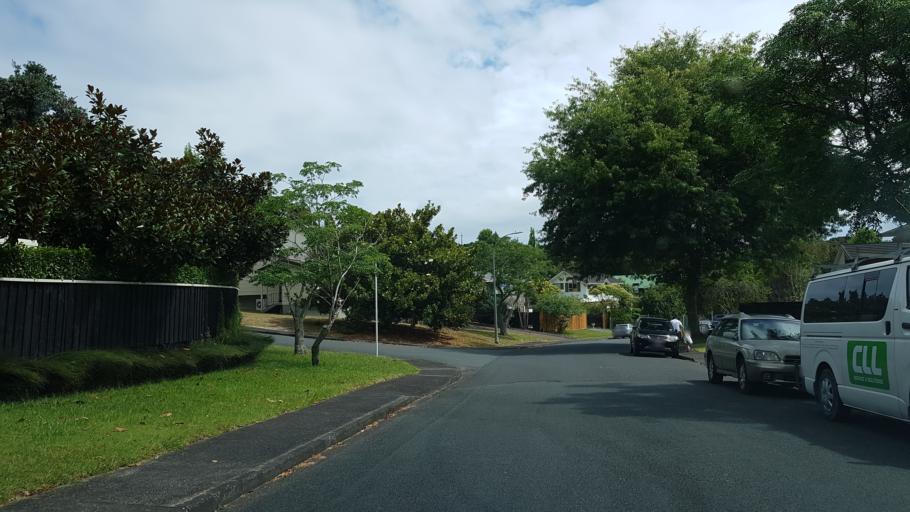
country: NZ
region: Auckland
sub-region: Auckland
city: North Shore
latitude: -36.7736
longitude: 174.7067
